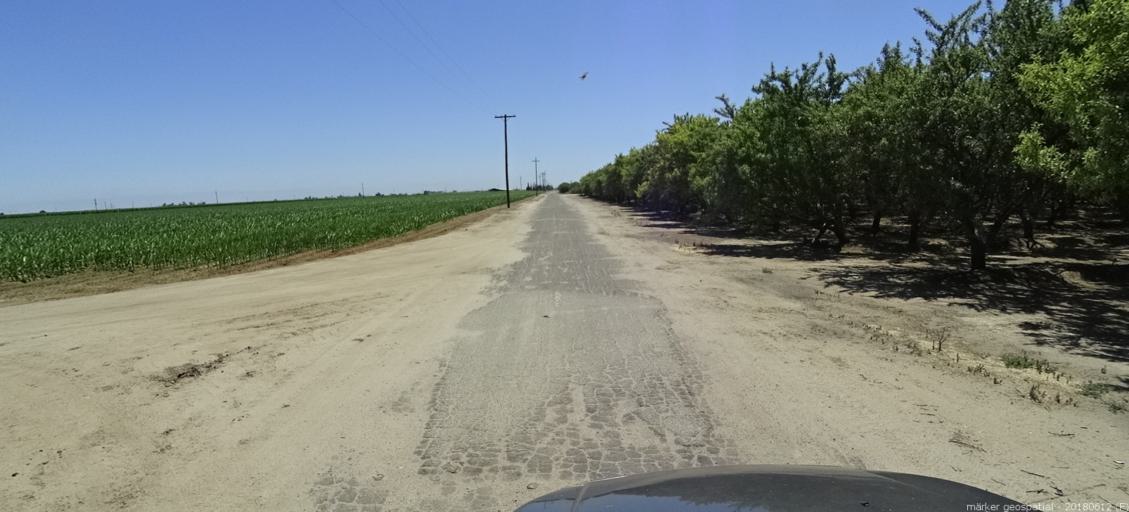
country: US
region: California
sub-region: Madera County
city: Chowchilla
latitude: 37.0616
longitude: -120.3603
